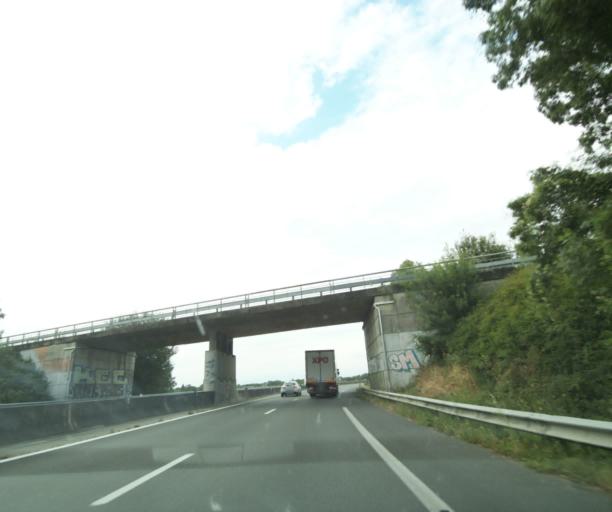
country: FR
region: Poitou-Charentes
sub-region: Departement de la Charente-Maritime
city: Aytre
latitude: 46.1232
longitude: -1.1097
